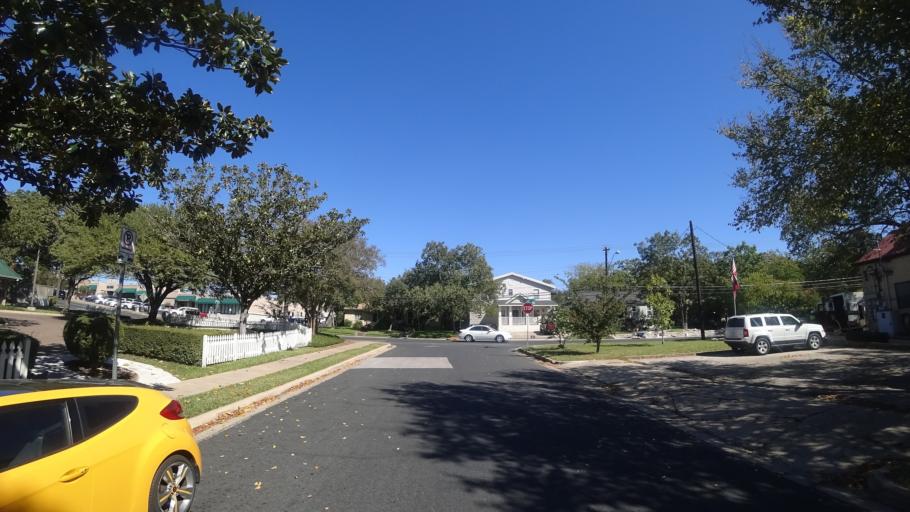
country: US
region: Texas
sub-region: Travis County
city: Rollingwood
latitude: 30.2956
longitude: -97.7675
